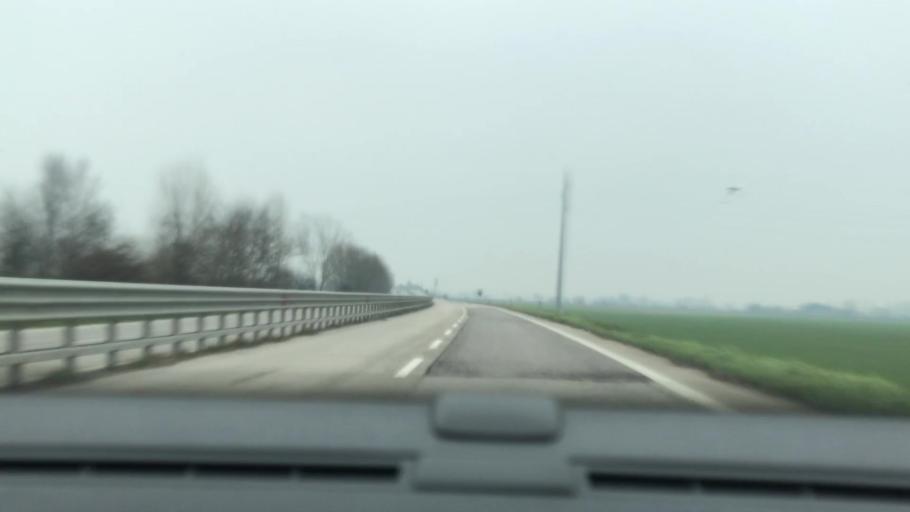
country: IT
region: Veneto
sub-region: Provincia di Rovigo
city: Arqua Polesine
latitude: 45.0251
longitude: 11.7487
